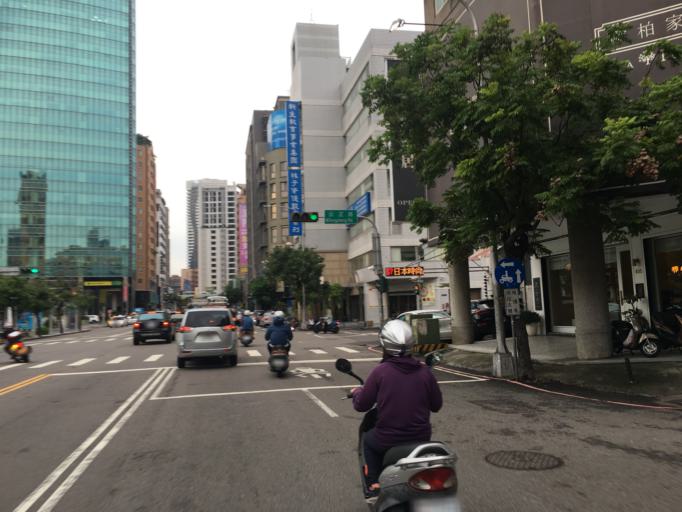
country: TW
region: Taiwan
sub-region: Taichung City
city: Taichung
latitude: 24.1487
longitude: 120.6654
